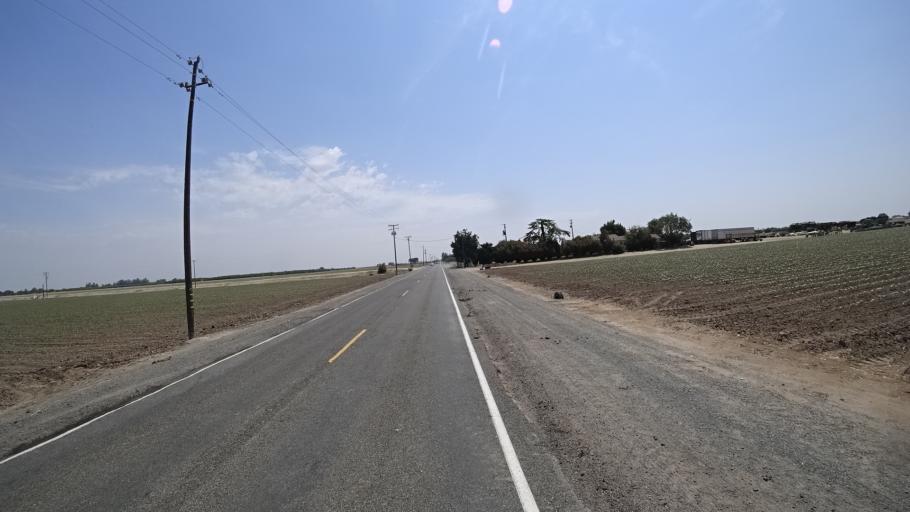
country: US
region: California
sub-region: Kings County
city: Lemoore
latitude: 36.3280
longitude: -119.8004
